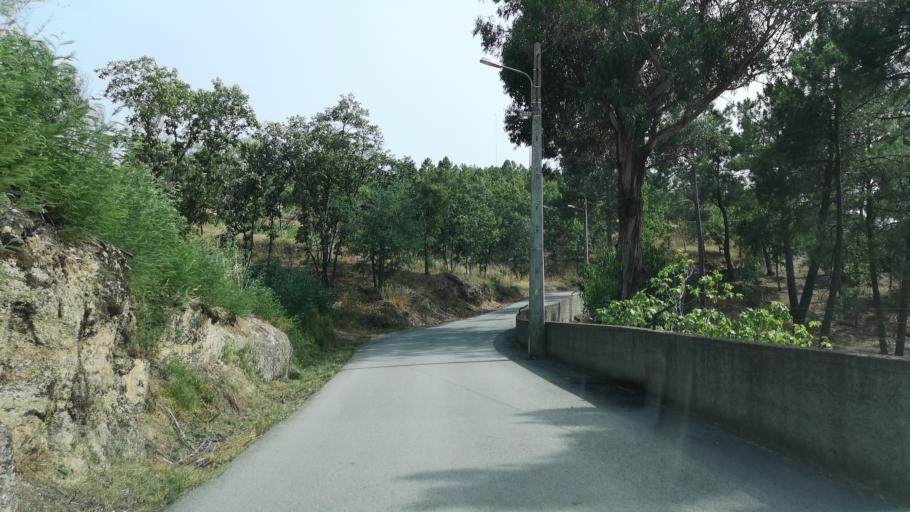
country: PT
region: Castelo Branco
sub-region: Belmonte
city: Belmonte
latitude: 40.3477
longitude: -7.3578
